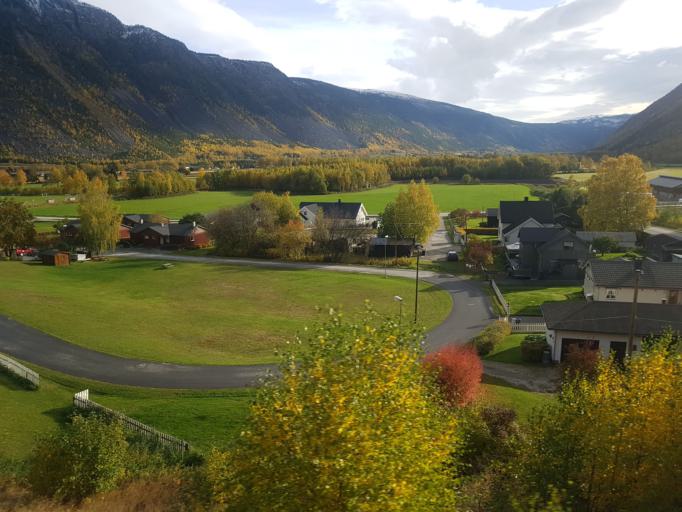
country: NO
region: Oppland
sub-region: Sel
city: Otta
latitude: 61.8417
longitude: 9.4029
